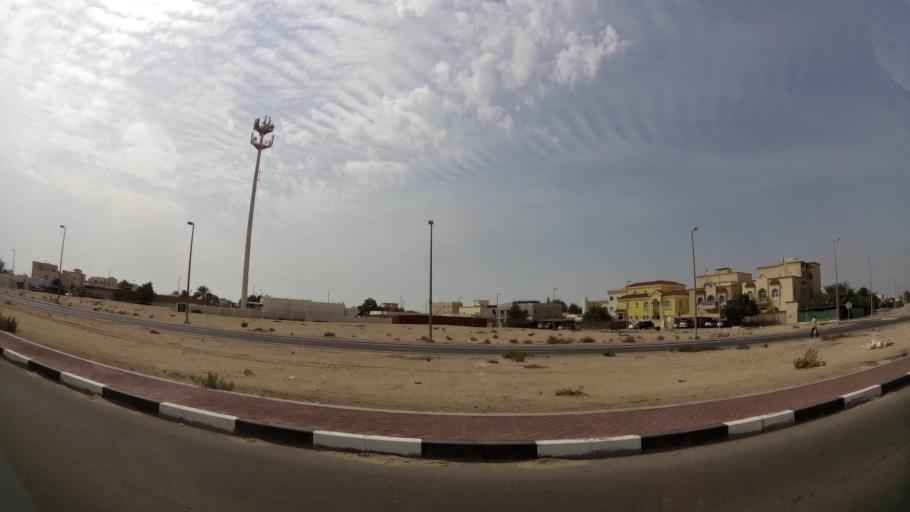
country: AE
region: Abu Dhabi
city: Abu Dhabi
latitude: 24.5453
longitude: 54.6845
